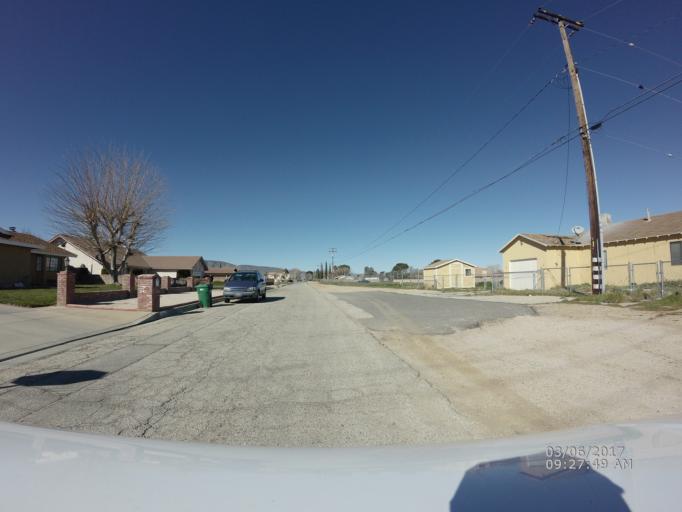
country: US
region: California
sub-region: Los Angeles County
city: Quartz Hill
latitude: 34.6566
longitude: -118.2190
